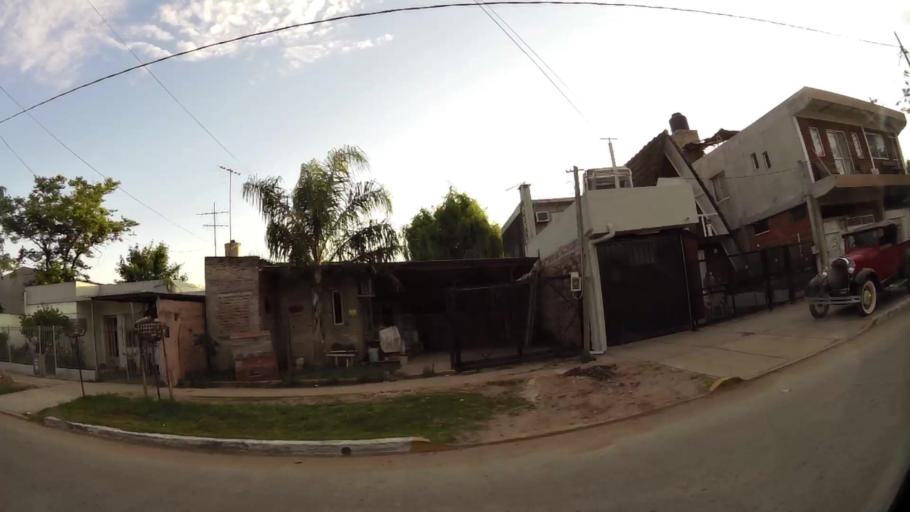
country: AR
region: Buenos Aires
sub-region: Partido de Merlo
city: Merlo
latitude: -34.6711
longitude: -58.7714
